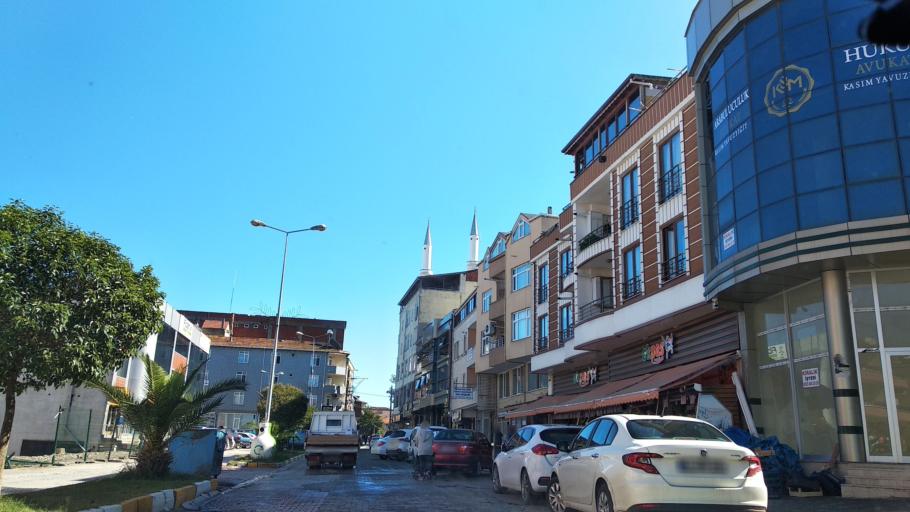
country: TR
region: Sakarya
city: Karasu
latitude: 41.0941
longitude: 30.6888
